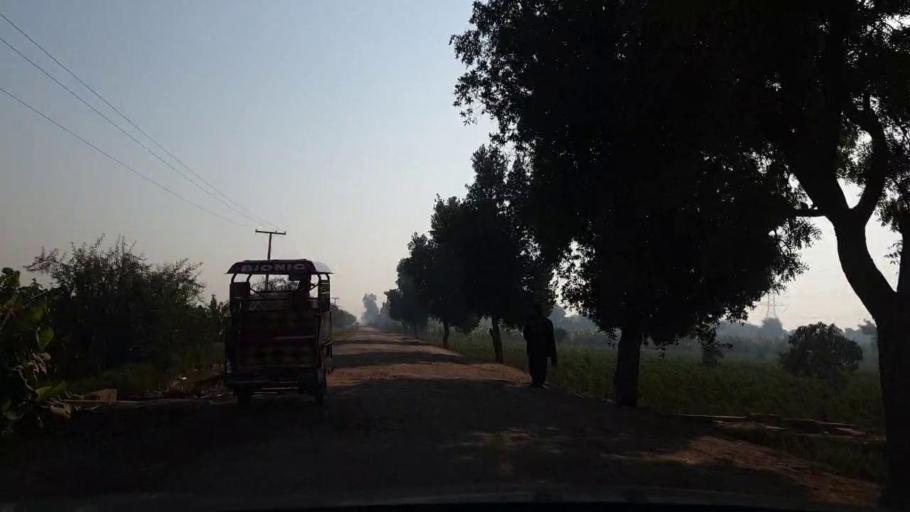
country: PK
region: Sindh
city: Tando Allahyar
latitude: 25.4919
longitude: 68.7179
